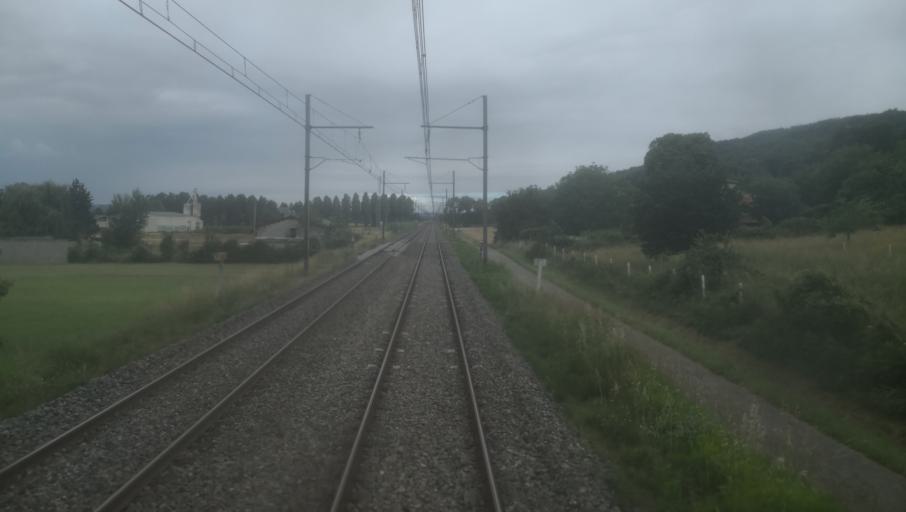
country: FR
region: Aquitaine
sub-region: Departement du Lot-et-Garonne
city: Port-Sainte-Marie
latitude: 44.2554
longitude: 0.3723
